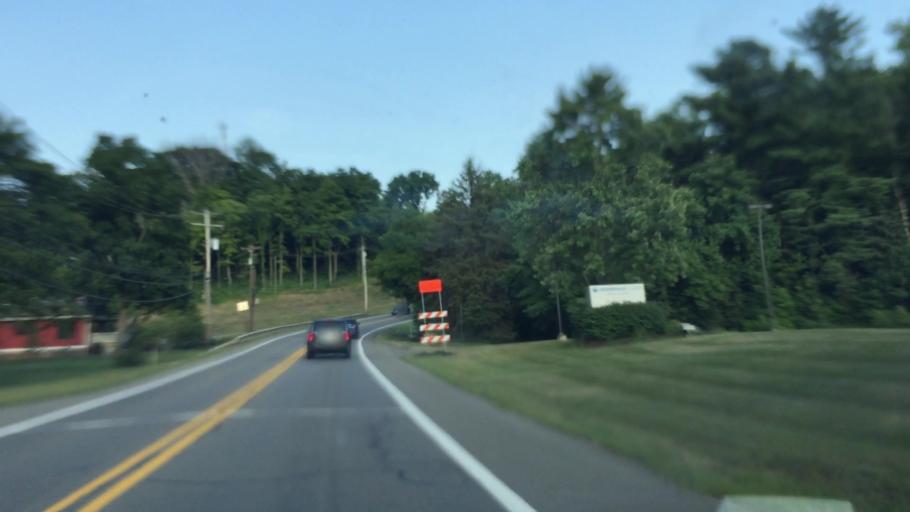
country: US
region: Pennsylvania
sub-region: Washington County
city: Thompsonville
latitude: 40.3179
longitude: -80.1109
